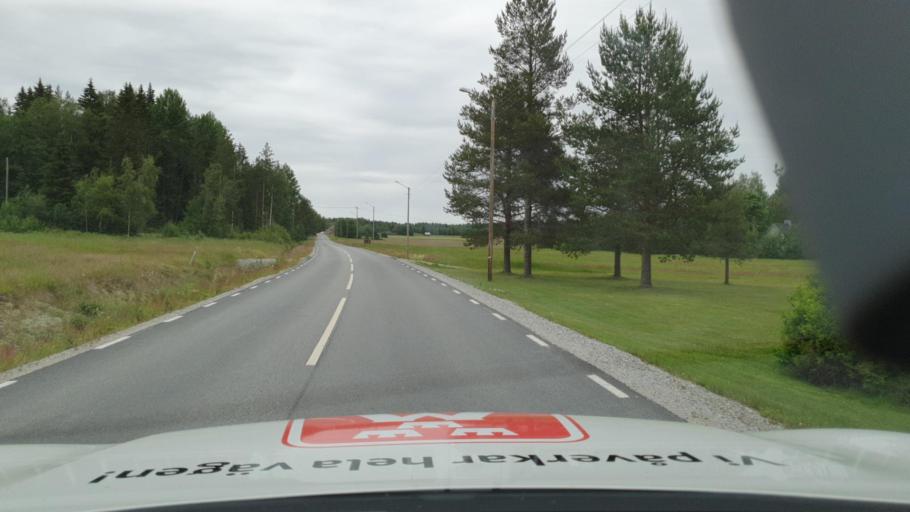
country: SE
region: Vaesterbotten
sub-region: Nordmalings Kommun
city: Nordmaling
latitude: 63.5086
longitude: 19.3356
